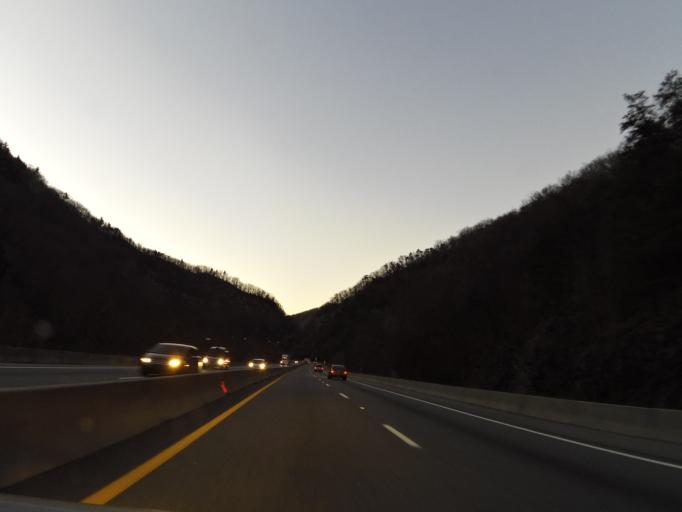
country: US
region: North Carolina
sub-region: Haywood County
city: Cove Creek
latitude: 35.7613
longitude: -83.0741
